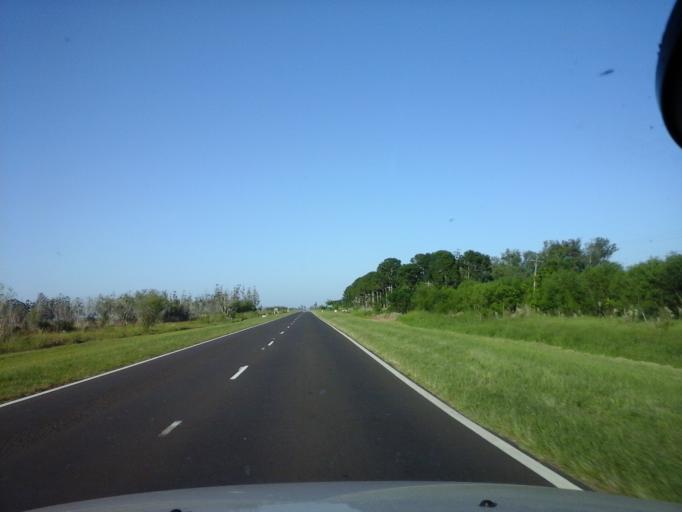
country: AR
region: Corrientes
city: Ita Ibate
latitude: -27.4472
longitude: -57.3961
